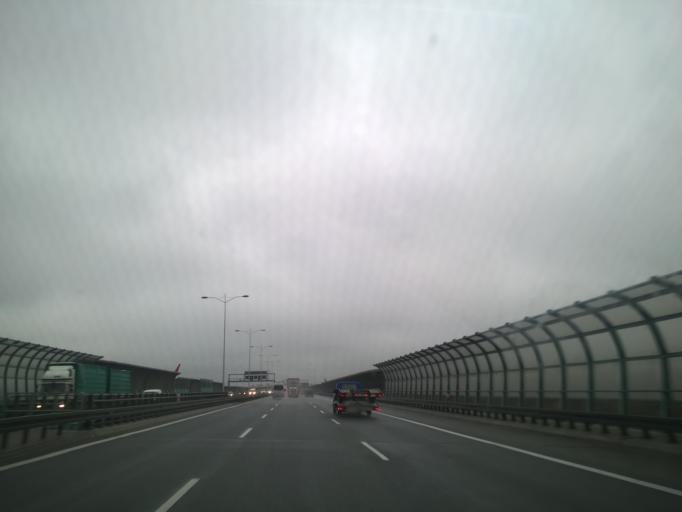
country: PL
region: Lower Silesian Voivodeship
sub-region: Powiat wroclawski
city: Smolec
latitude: 51.0944
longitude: 16.9316
